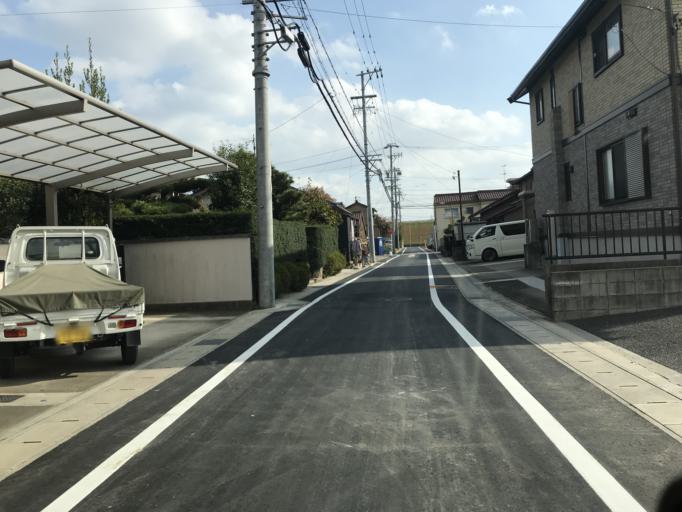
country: JP
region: Aichi
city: Nagoya-shi
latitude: 35.1889
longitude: 136.8506
